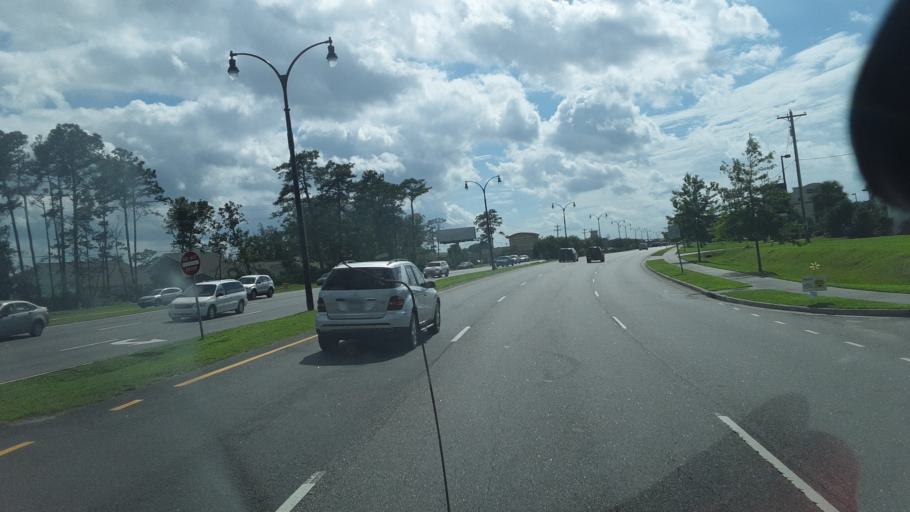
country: US
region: South Carolina
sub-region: Horry County
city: North Myrtle Beach
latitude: 33.8456
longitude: -78.6548
